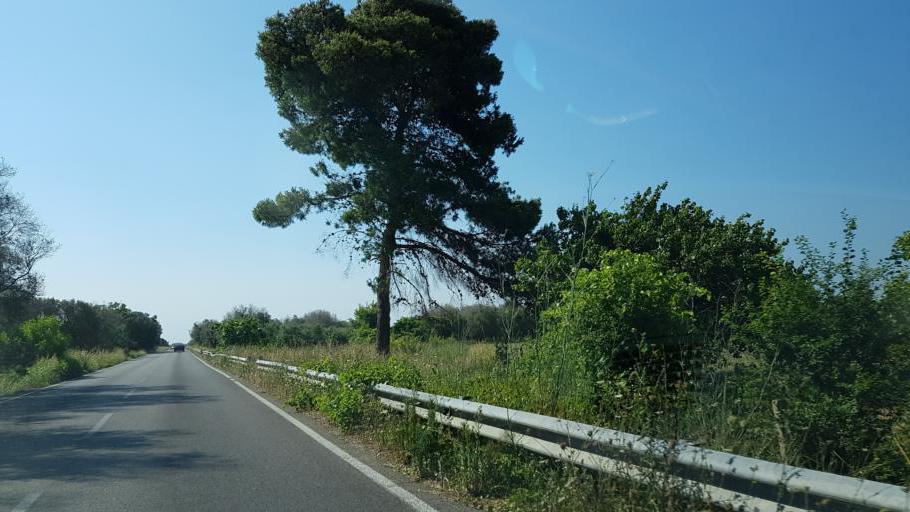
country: IT
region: Apulia
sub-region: Provincia di Brindisi
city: San Donaci
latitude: 40.4326
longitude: 17.9385
